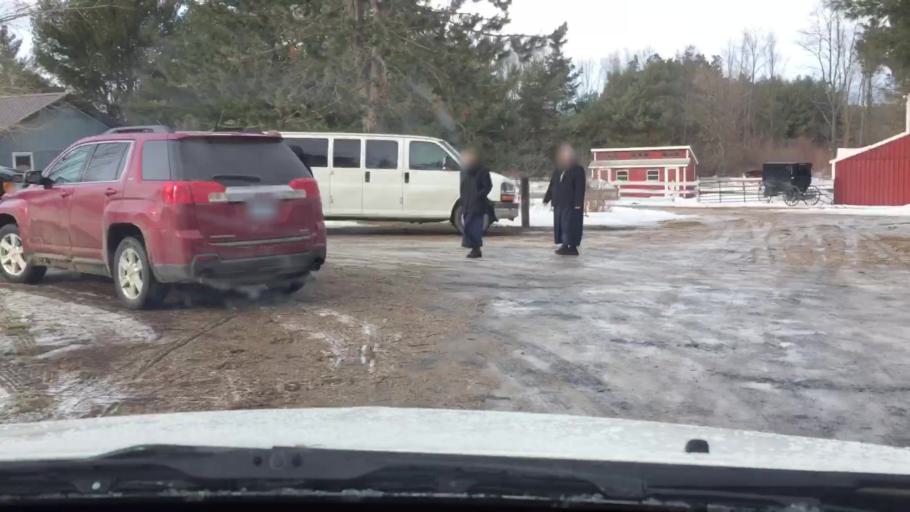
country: US
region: Michigan
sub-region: Wexford County
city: Manton
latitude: 44.4037
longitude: -85.4348
